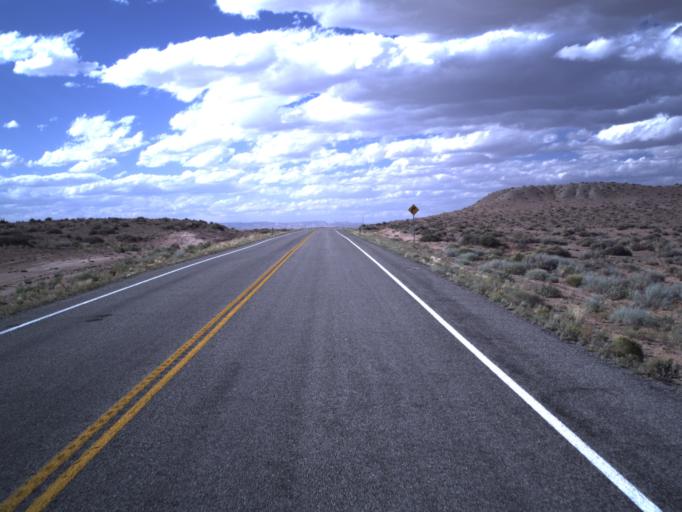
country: US
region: Utah
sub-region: Emery County
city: Ferron
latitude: 38.3363
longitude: -110.6862
